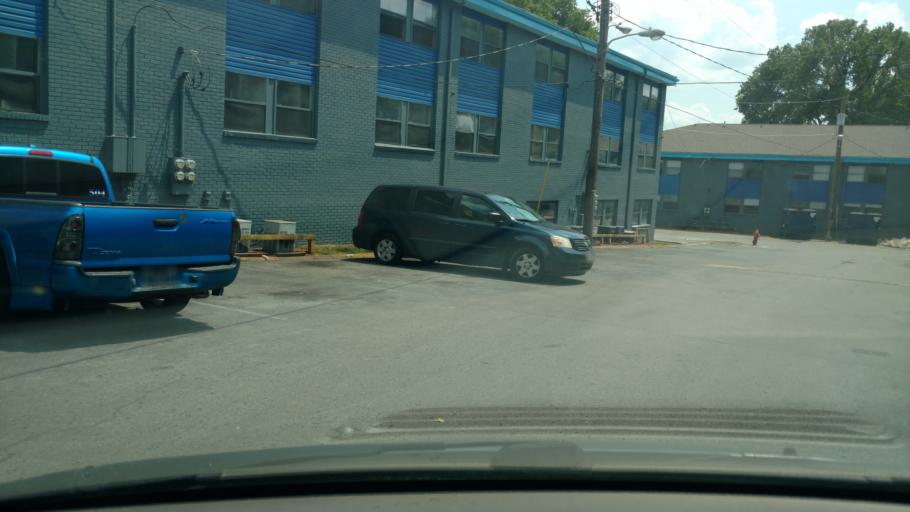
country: US
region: Tennessee
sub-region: Davidson County
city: Nashville
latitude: 36.2004
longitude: -86.7377
